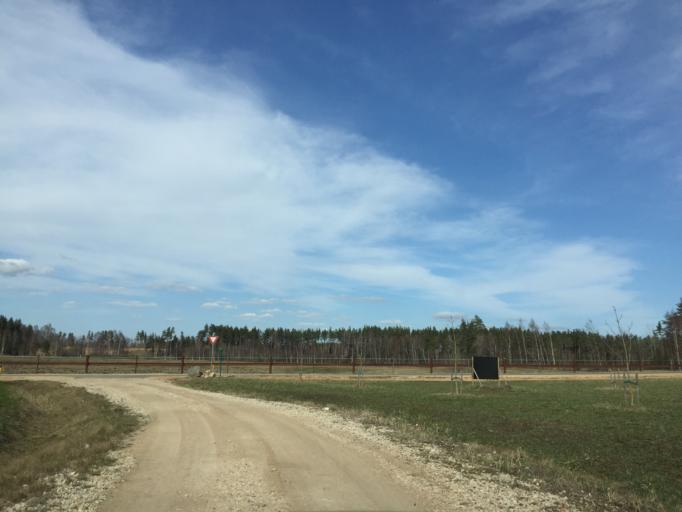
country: LV
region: Ikskile
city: Ikskile
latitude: 56.8416
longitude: 24.5303
